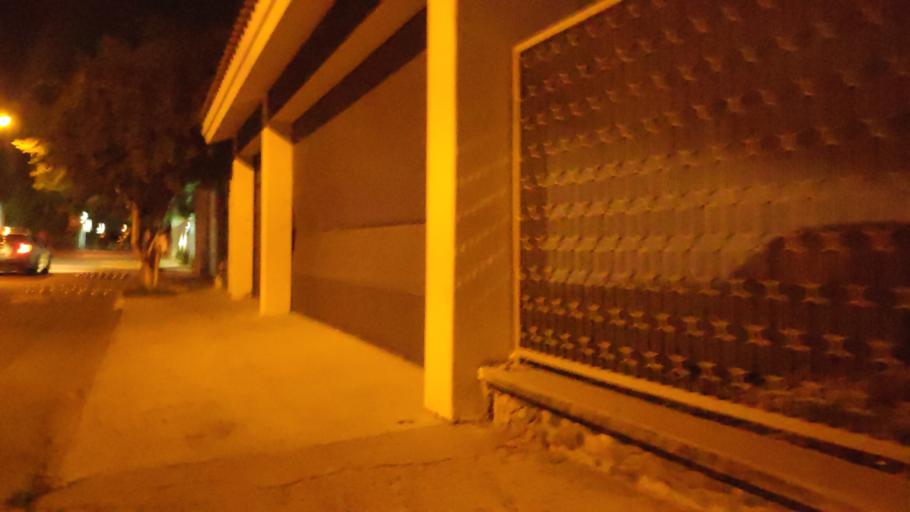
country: MX
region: Sinaloa
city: Culiacan
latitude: 24.7962
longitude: -107.3953
